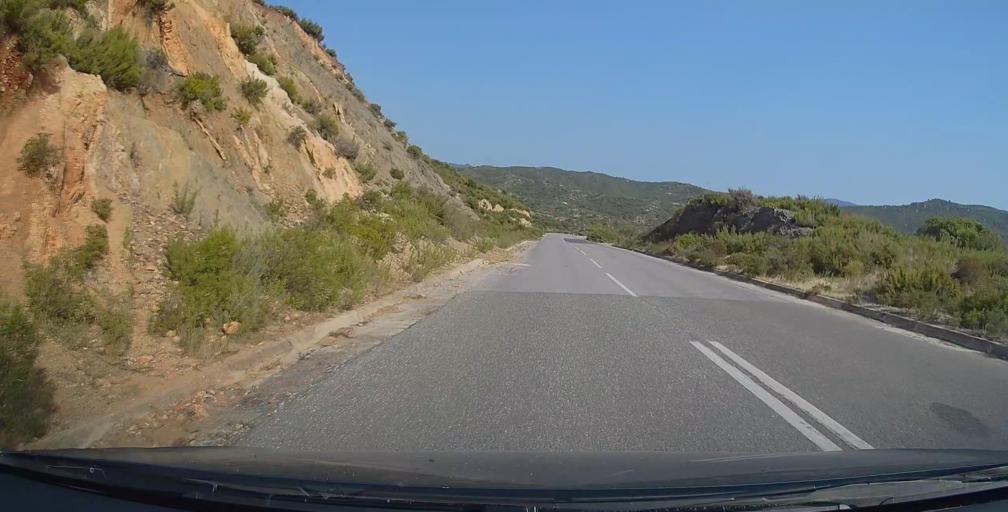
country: GR
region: Central Macedonia
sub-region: Nomos Chalkidikis
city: Sykia
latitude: 39.9883
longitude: 23.9593
